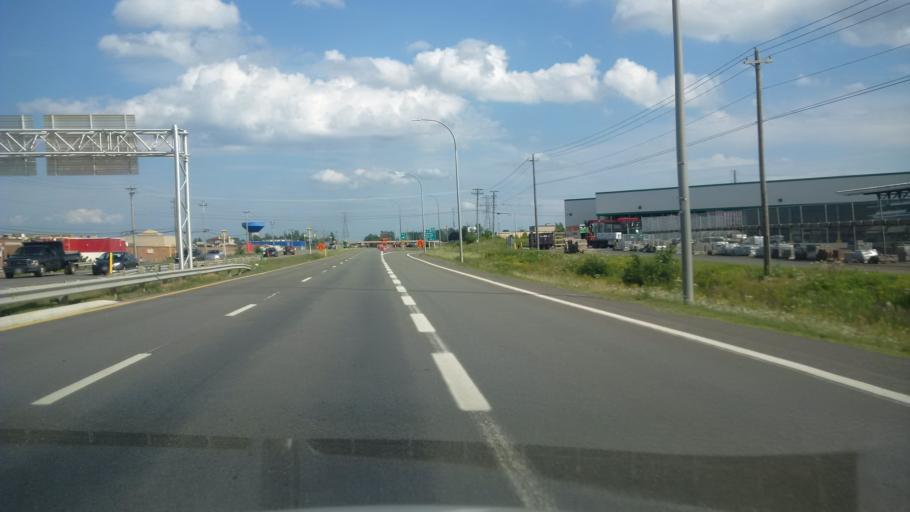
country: CA
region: New Brunswick
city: Fredericton
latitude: 45.9399
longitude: -66.6677
